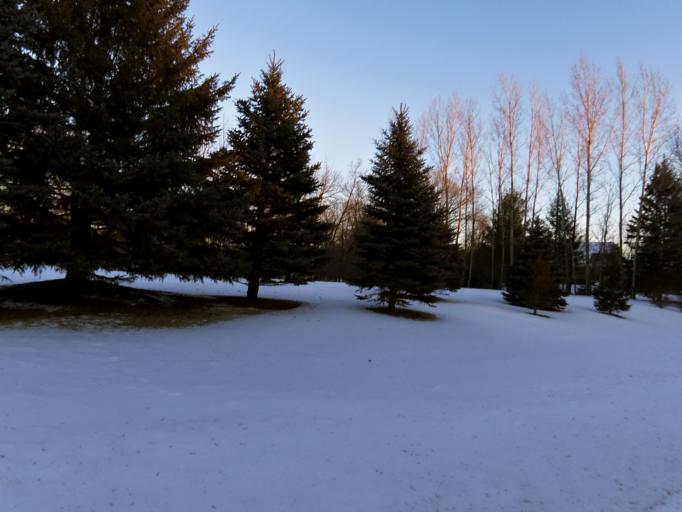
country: US
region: Minnesota
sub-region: Washington County
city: Lakeland
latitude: 44.9656
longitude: -92.8086
